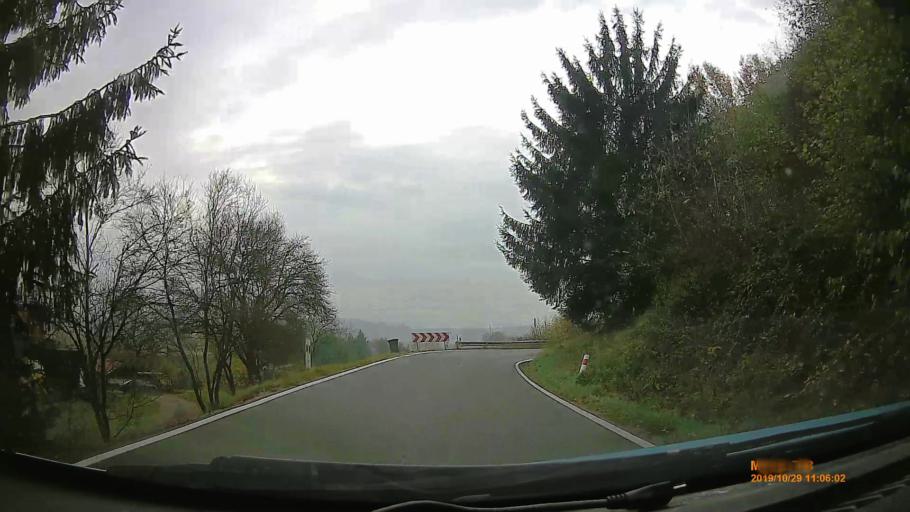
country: PL
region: Lower Silesian Voivodeship
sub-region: Powiat klodzki
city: Szczytna
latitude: 50.4663
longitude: 16.4791
